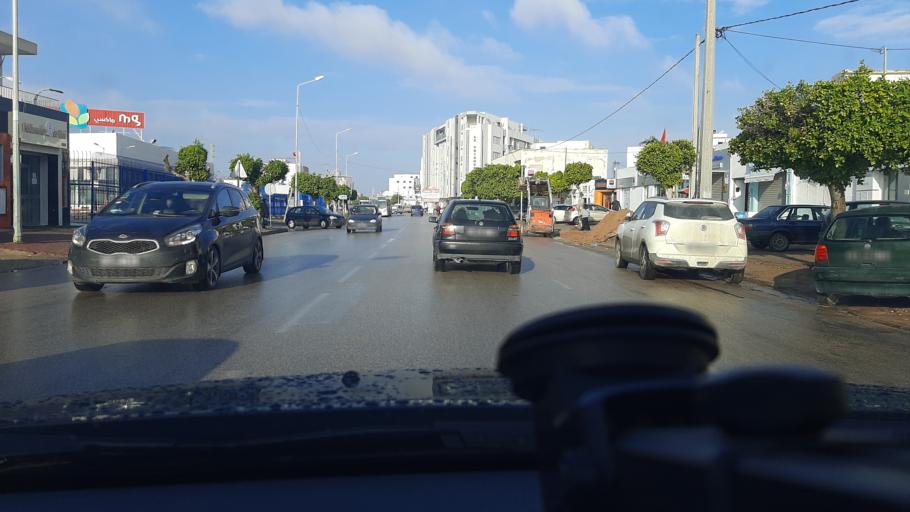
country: TN
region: Safaqis
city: Sfax
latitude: 34.7467
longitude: 10.7249
